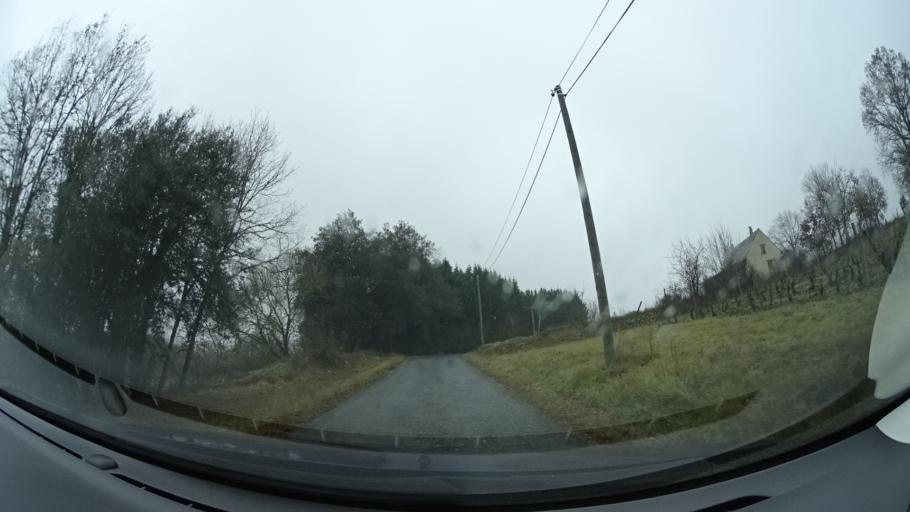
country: FR
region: Aquitaine
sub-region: Departement de la Dordogne
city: Cenac-et-Saint-Julien
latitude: 44.7348
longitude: 1.1567
